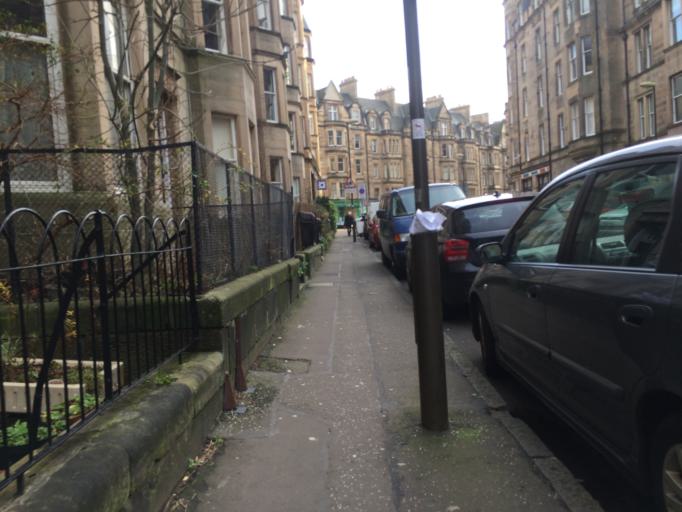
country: GB
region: Scotland
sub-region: Edinburgh
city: Edinburgh
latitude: 55.9363
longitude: -3.2106
